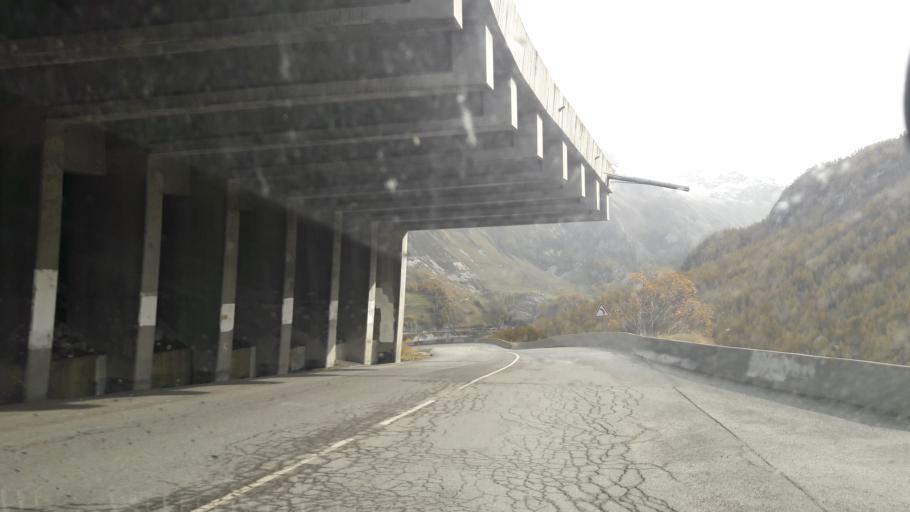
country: FR
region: Rhone-Alpes
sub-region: Departement de la Savoie
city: Tignes
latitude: 45.4756
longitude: 6.9155
